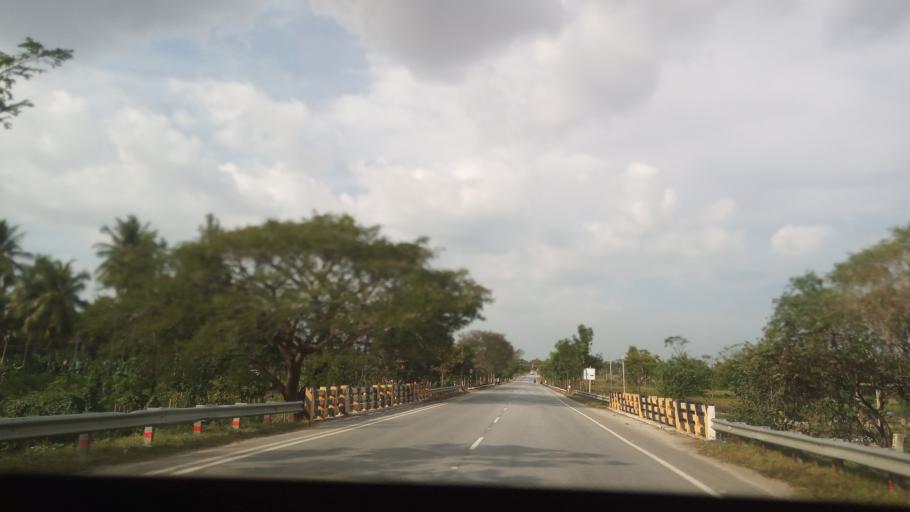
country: IN
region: Karnataka
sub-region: Tumkur
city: Kunigal
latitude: 12.8571
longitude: 77.0389
